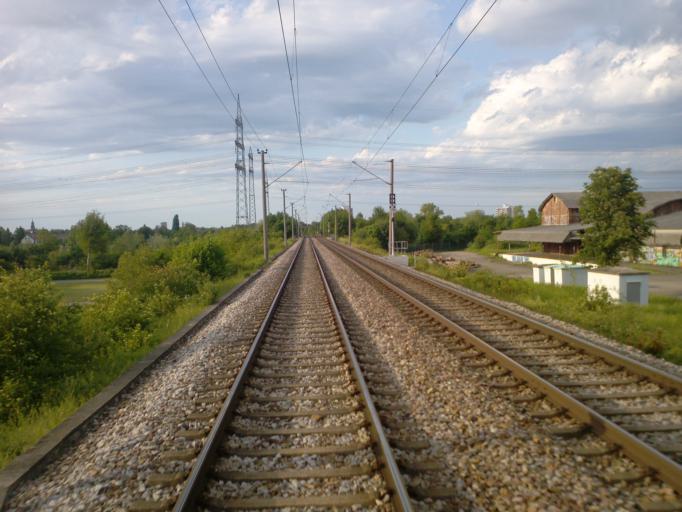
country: DE
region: Baden-Wuerttemberg
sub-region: Karlsruhe Region
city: Ettlingen
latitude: 48.9575
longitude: 8.4035
